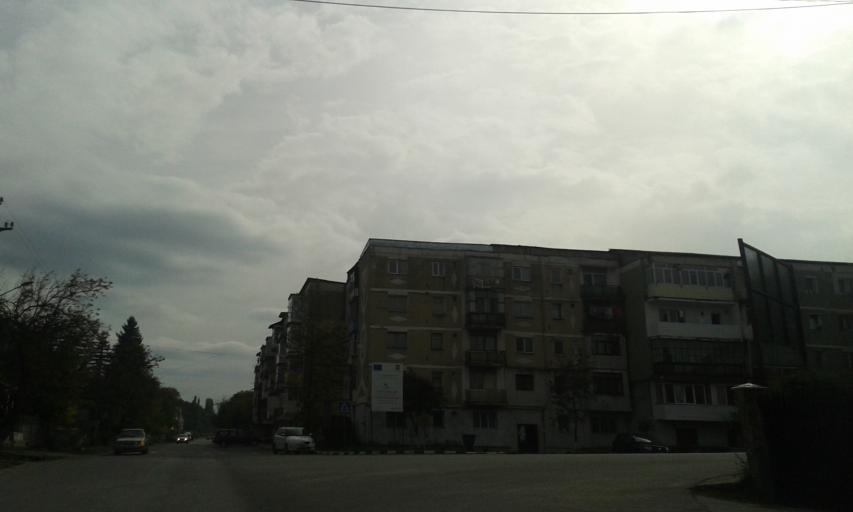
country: RO
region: Gorj
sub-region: Comuna Targu Carbunesti
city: Targu Carbunesti
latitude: 44.9640
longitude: 23.5067
